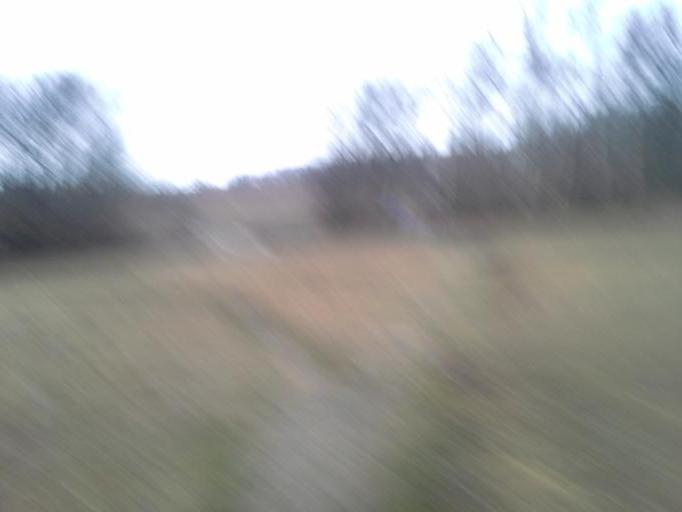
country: RU
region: Moscow
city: Yasenevo
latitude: 55.5804
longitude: 37.5392
